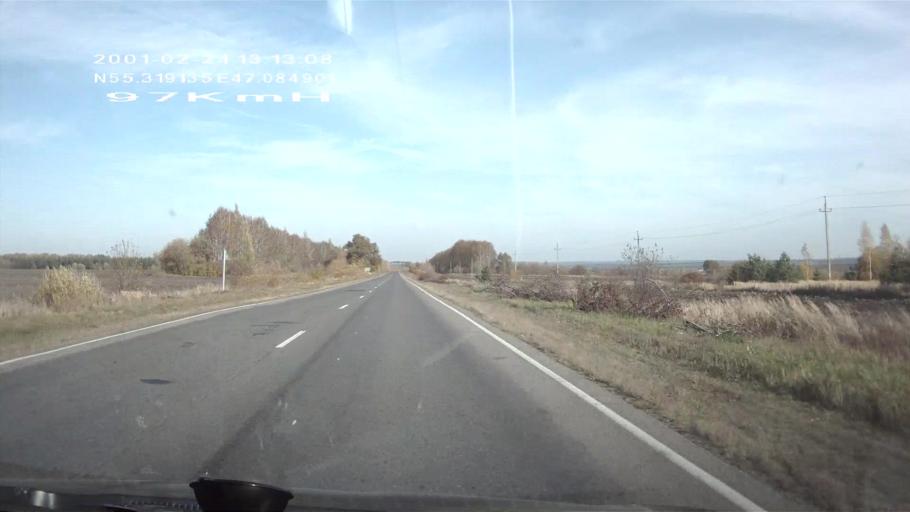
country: RU
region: Chuvashia
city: Ibresi
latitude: 55.3191
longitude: 47.0853
